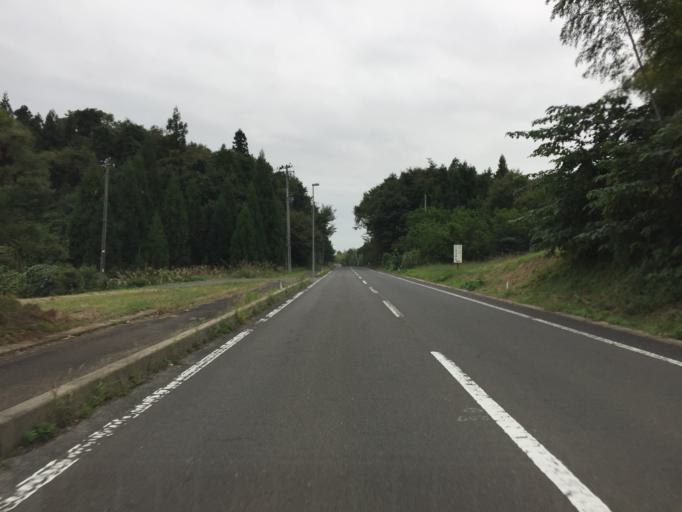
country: JP
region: Fukushima
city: Fukushima-shi
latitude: 37.6698
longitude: 140.4788
